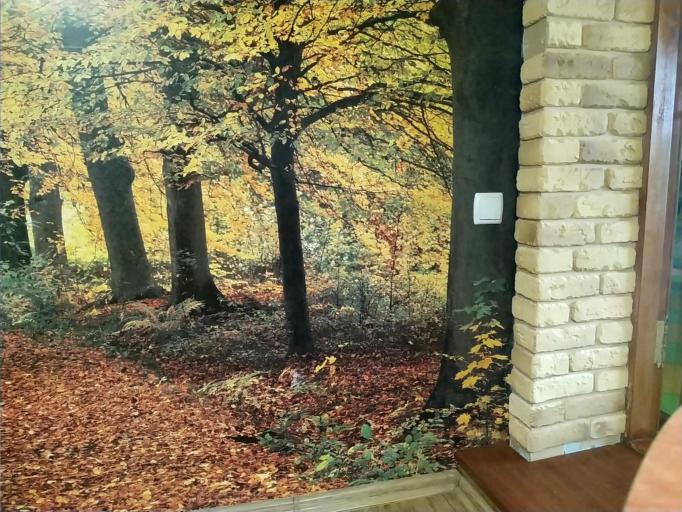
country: RU
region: Smolensk
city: Dorogobuzh
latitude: 54.8461
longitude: 33.3249
